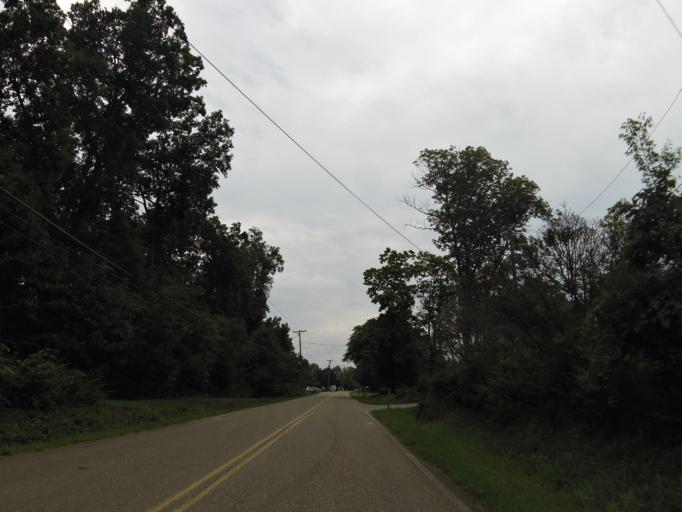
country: US
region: Tennessee
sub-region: Sevier County
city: Seymour
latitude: 35.9202
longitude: -83.8193
